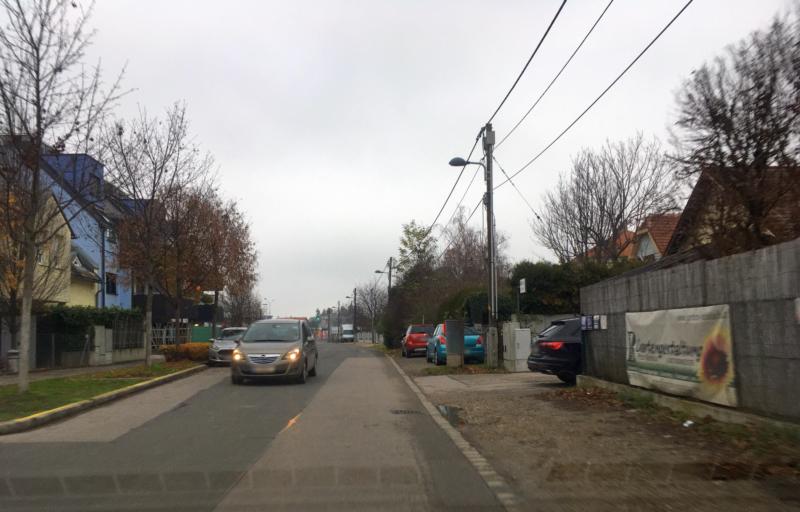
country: AT
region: Lower Austria
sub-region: Politischer Bezirk Ganserndorf
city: Gross-Enzersdorf
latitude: 48.2157
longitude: 16.4926
